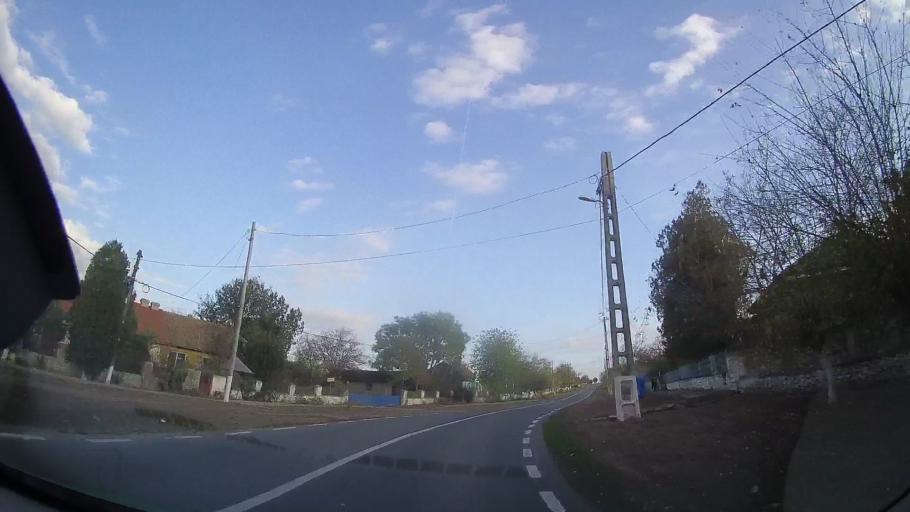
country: RO
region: Constanta
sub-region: Comuna Chirnogeni
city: Plopeni
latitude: 43.9617
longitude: 28.1419
